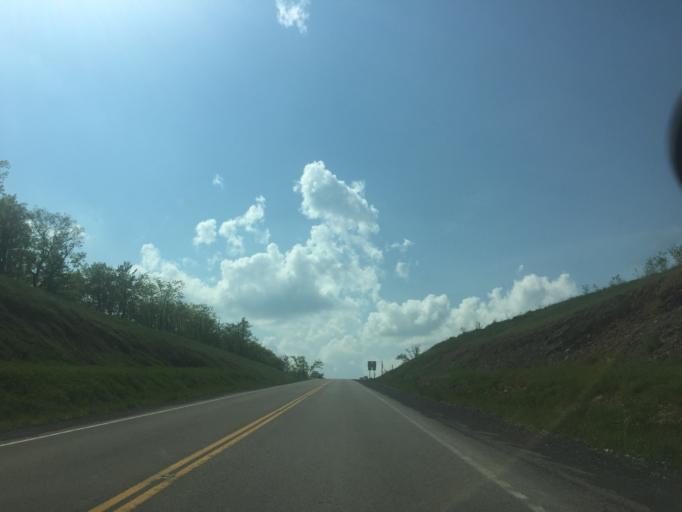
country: US
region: West Virginia
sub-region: Grant County
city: Petersburg
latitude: 39.2165
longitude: -79.2072
